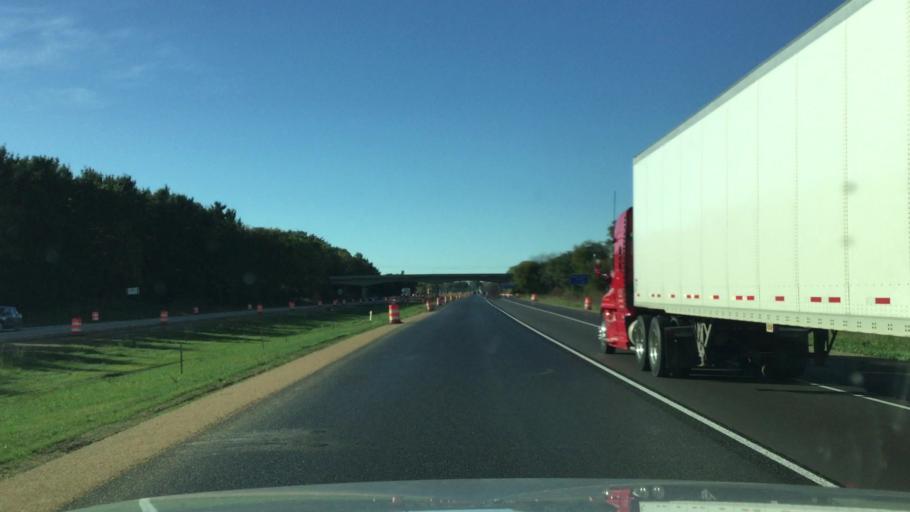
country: US
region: Michigan
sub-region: Calhoun County
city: Marshall
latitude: 42.2865
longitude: -84.9517
